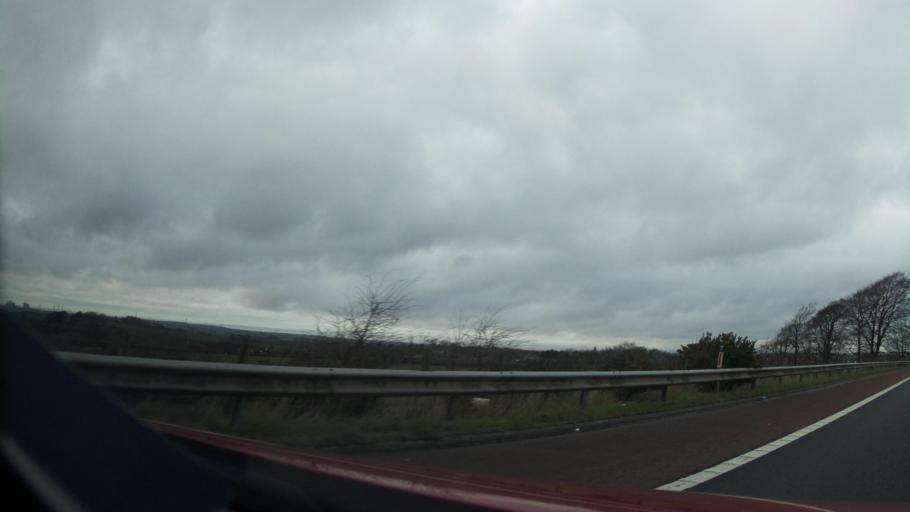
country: GB
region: England
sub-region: Lancashire
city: Lancaster
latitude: 54.0191
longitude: -2.7821
